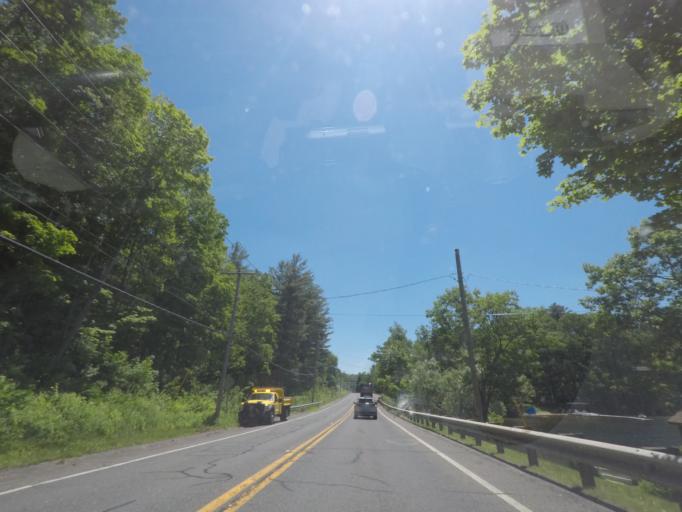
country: US
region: Massachusetts
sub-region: Berkshire County
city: Becket
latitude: 42.2820
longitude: -73.1434
